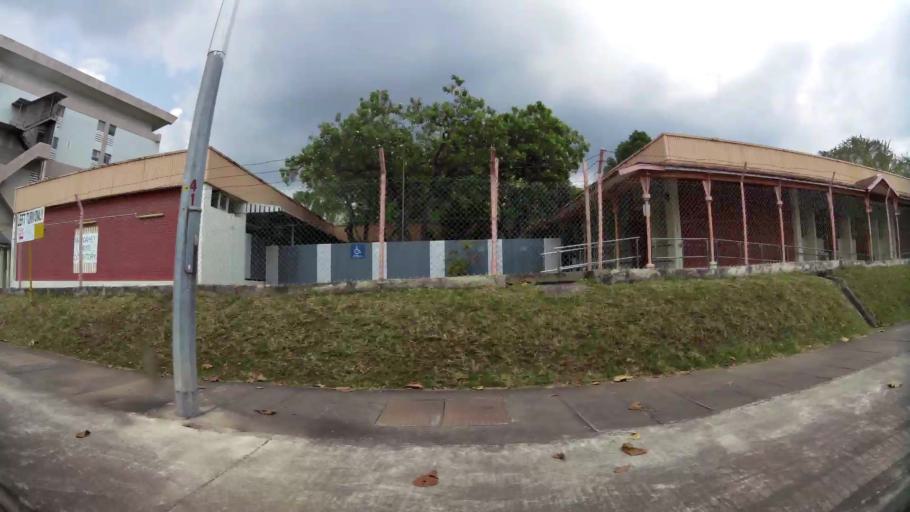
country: SG
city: Singapore
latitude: 1.2989
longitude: 103.8045
